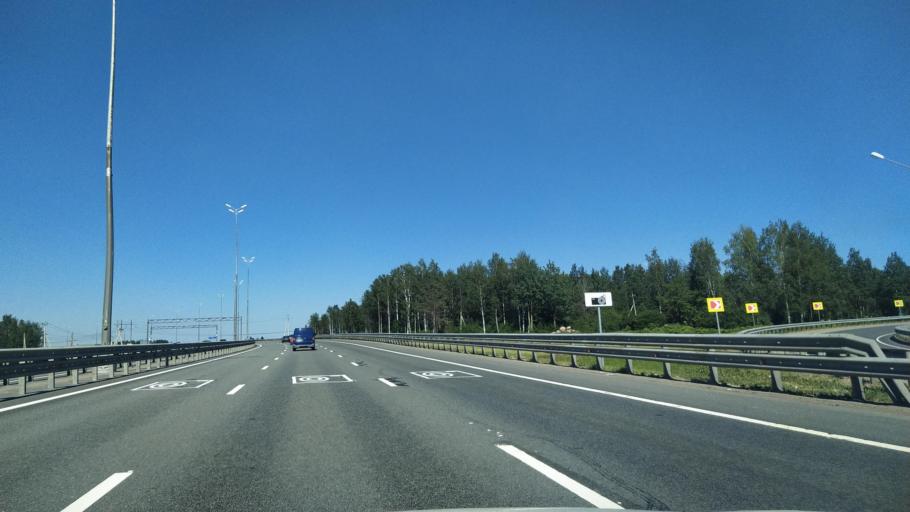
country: RU
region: Leningrad
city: Maloye Verevo
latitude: 59.5810
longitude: 30.1773
